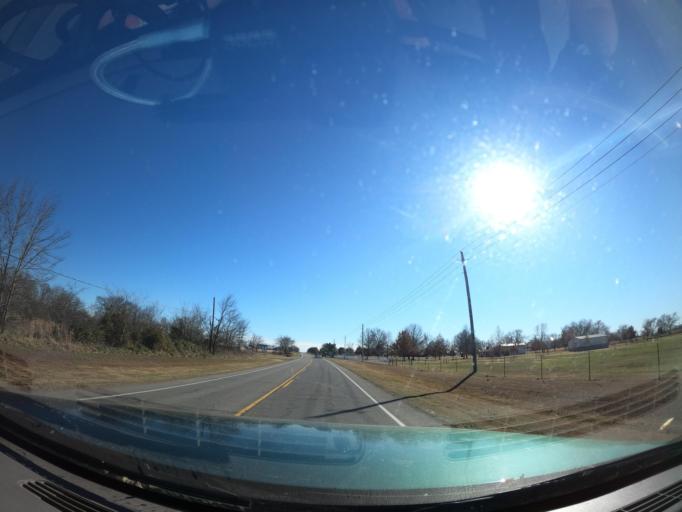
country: US
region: Oklahoma
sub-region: Muskogee County
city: Haskell
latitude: 35.8073
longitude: -95.6742
